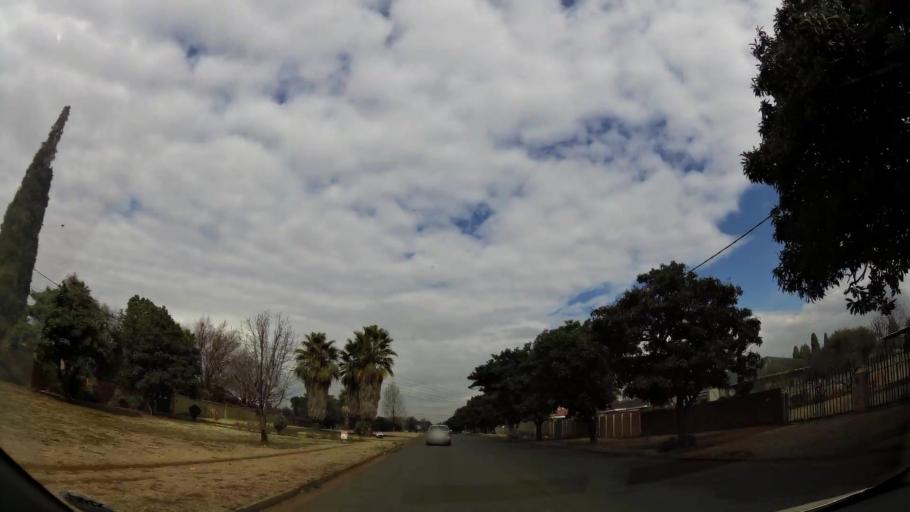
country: ZA
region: Gauteng
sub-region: Sedibeng District Municipality
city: Vereeniging
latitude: -26.6484
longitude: 27.9694
